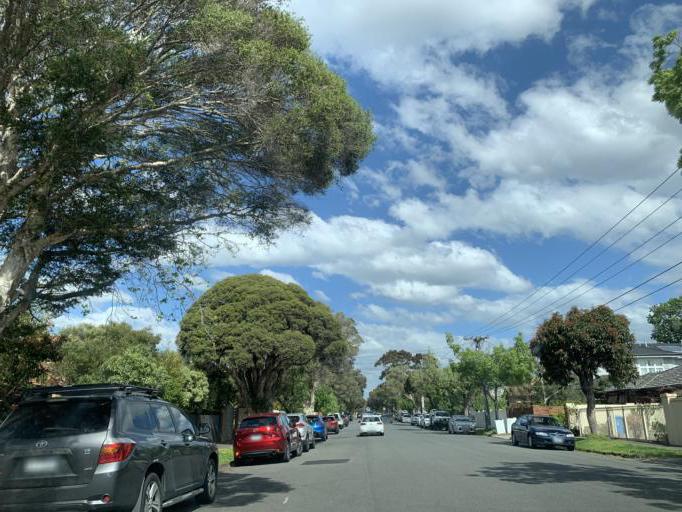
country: AU
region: Victoria
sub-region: Bayside
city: North Brighton
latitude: -37.9103
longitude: 145.0022
